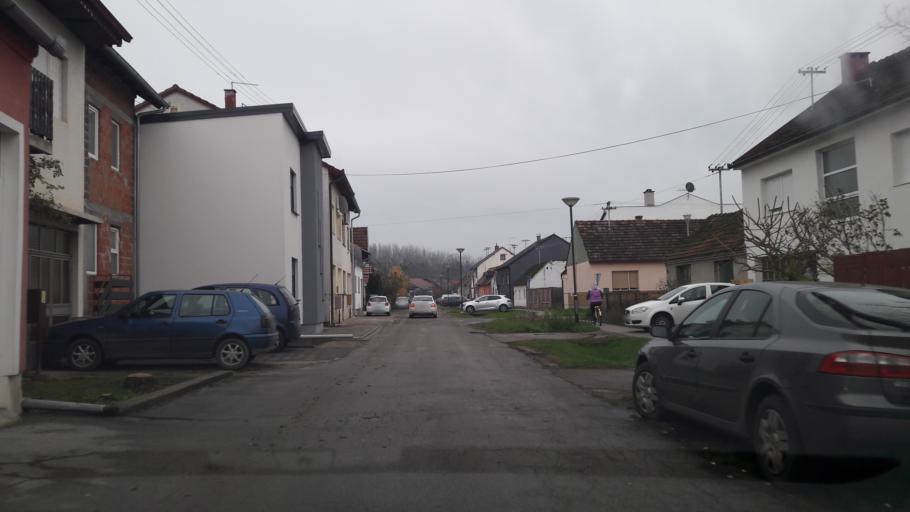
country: HR
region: Osjecko-Baranjska
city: Visnjevac
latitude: 45.5702
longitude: 18.6201
